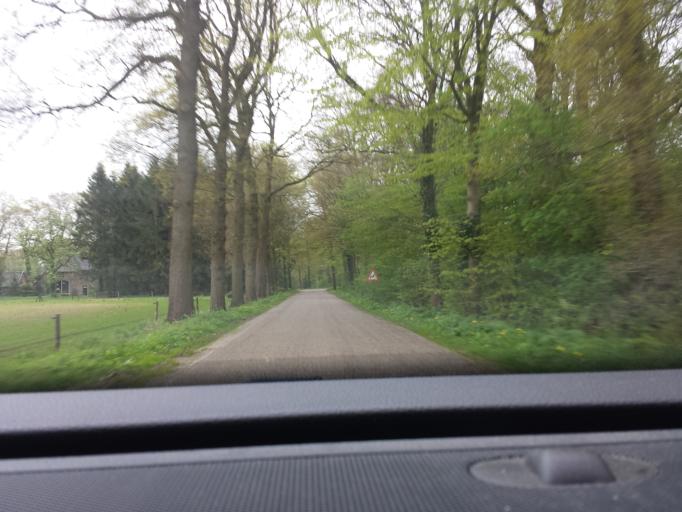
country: NL
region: Gelderland
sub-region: Gemeente Bronckhorst
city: Hengelo
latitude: 52.0907
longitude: 6.3529
